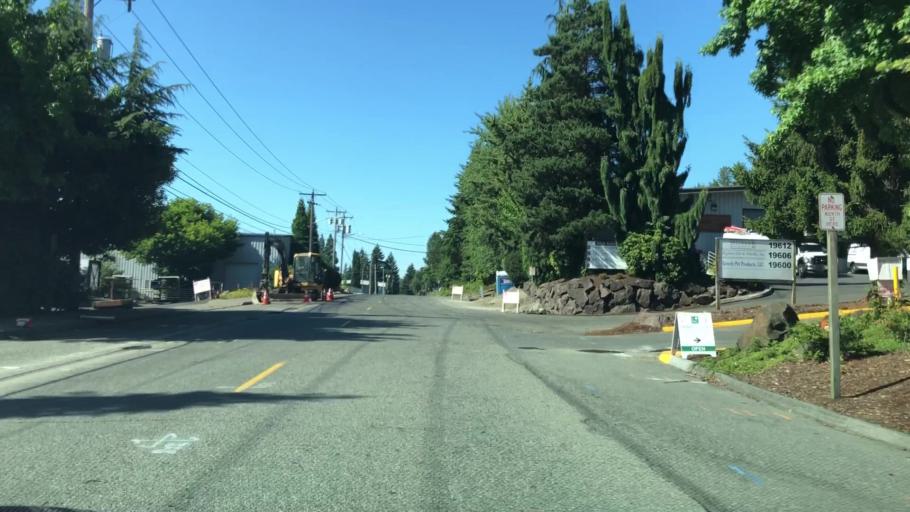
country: US
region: Washington
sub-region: King County
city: Woodinville
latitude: 47.7694
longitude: -122.1478
